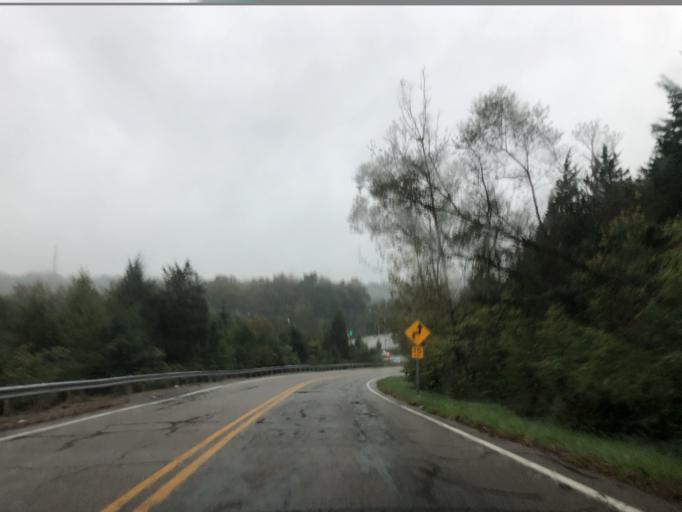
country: US
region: Ohio
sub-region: Hamilton County
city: The Village of Indian Hill
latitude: 39.2488
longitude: -84.2980
